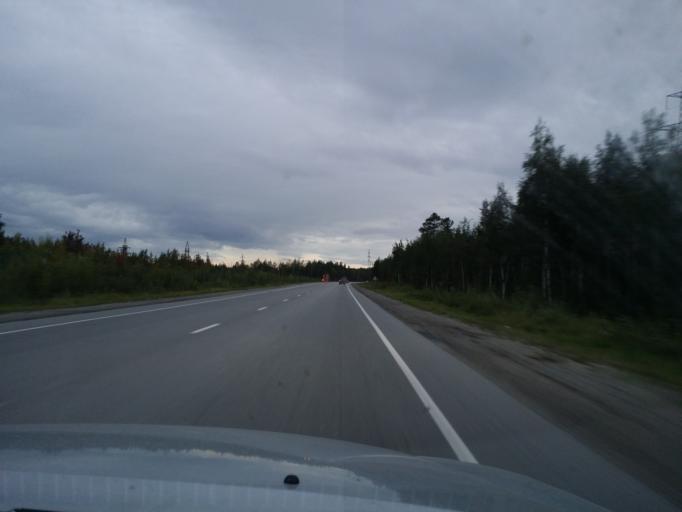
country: RU
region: Khanty-Mansiyskiy Avtonomnyy Okrug
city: Nizhnevartovsk
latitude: 60.9682
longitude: 76.6850
